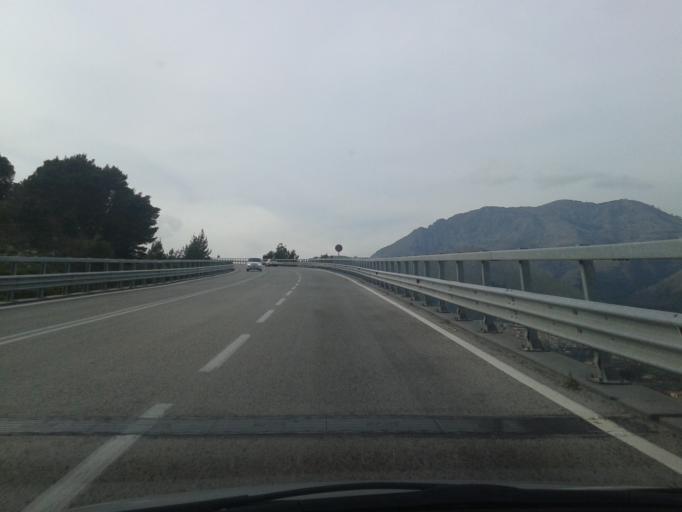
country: IT
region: Sicily
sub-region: Palermo
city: Giacalone
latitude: 38.0374
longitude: 13.2404
